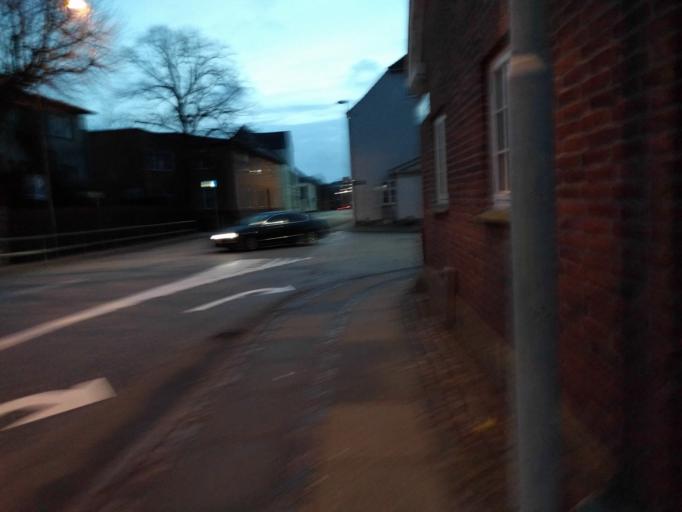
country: DK
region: North Denmark
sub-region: Alborg Kommune
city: Aalborg
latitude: 57.0600
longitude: 9.9226
